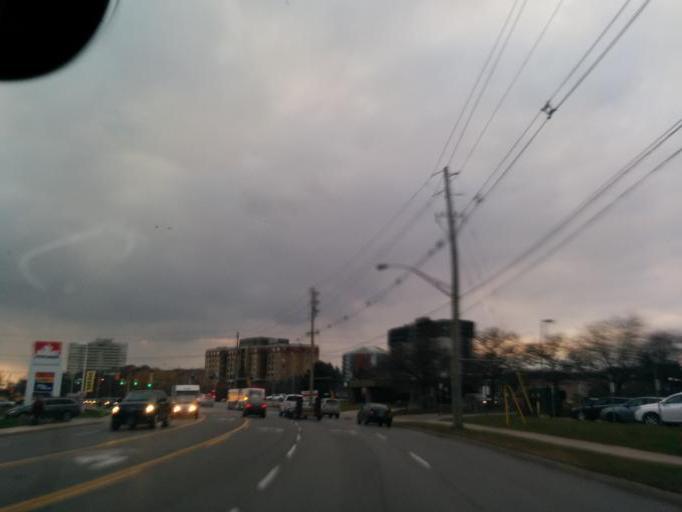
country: CA
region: Ontario
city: Oakville
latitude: 43.4652
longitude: -79.6856
